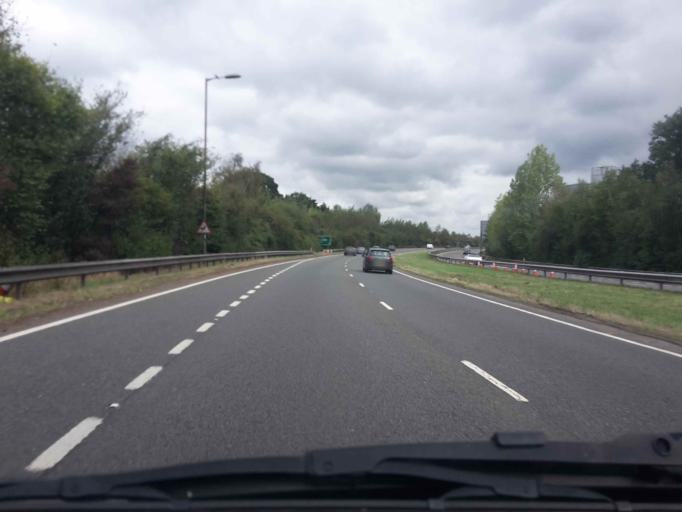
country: GB
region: England
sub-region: Hampshire
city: Farnborough
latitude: 51.2775
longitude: -0.7350
